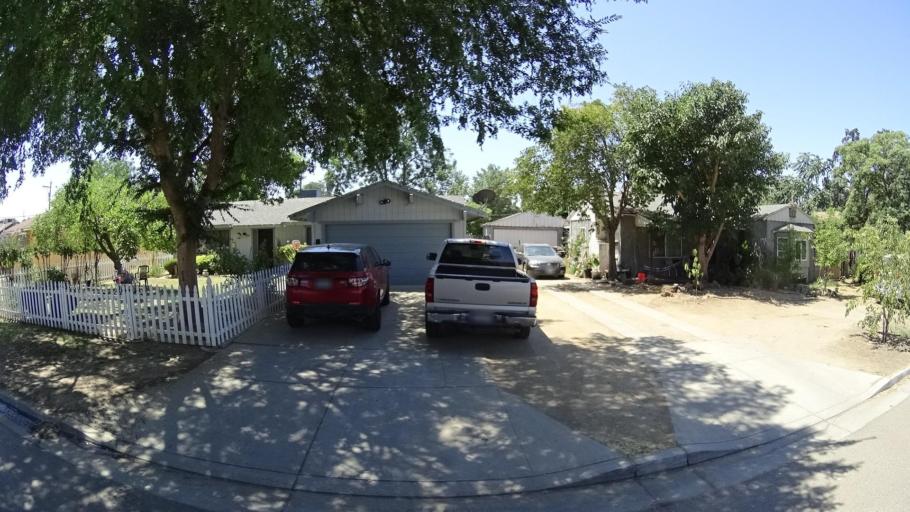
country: US
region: California
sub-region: Fresno County
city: Fresno
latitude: 36.7677
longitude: -119.7756
